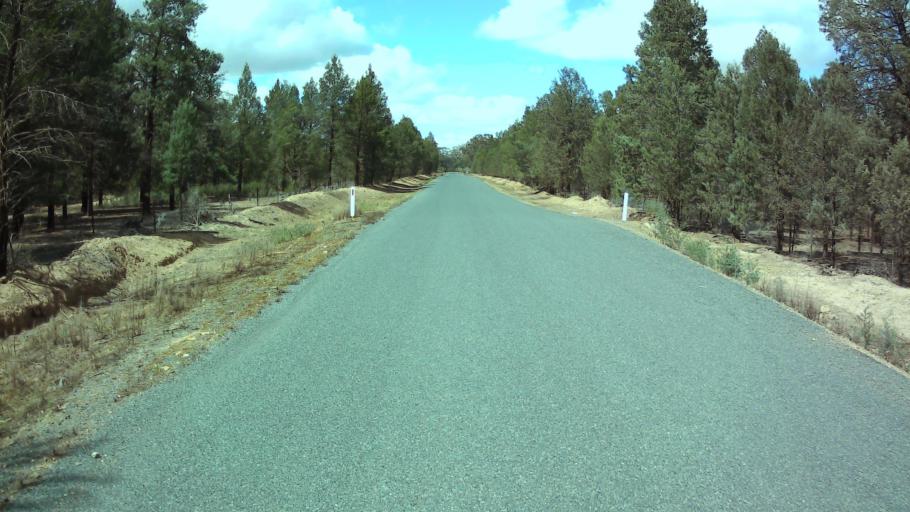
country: AU
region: New South Wales
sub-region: Weddin
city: Grenfell
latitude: -33.9026
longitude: 147.9204
